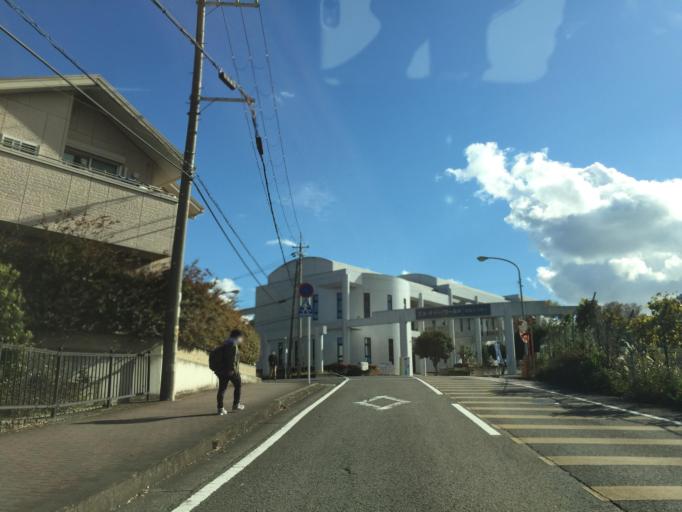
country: JP
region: Wakayama
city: Wakayama-shi
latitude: 34.2665
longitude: 135.1486
